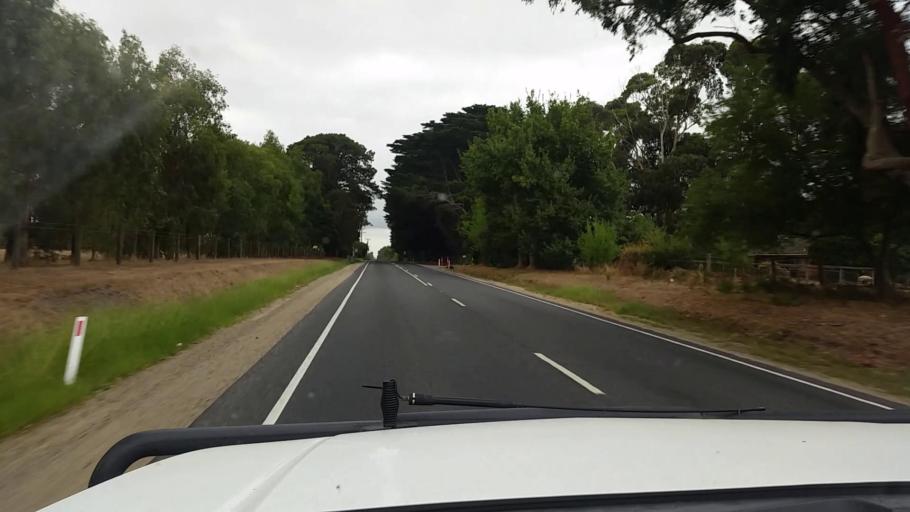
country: AU
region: Victoria
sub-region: Mornington Peninsula
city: Hastings
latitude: -38.2764
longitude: 145.1456
